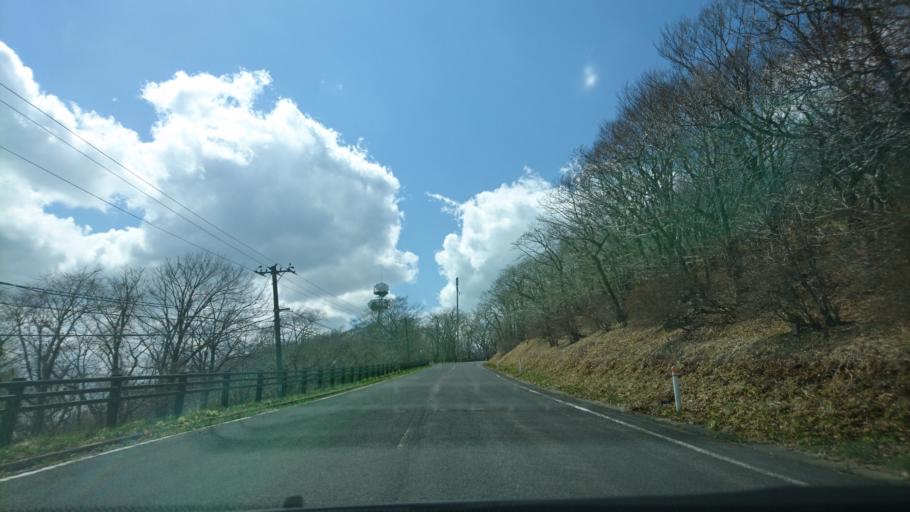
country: JP
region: Iwate
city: Ofunato
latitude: 38.9732
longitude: 141.4479
